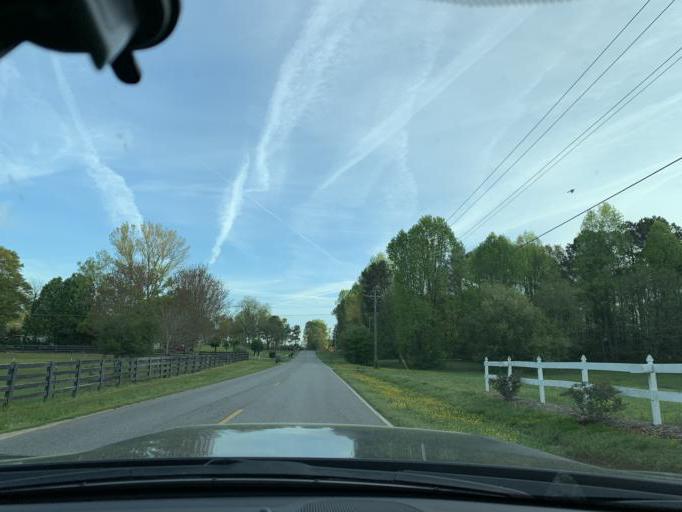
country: US
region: Georgia
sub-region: Forsyth County
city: Cumming
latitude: 34.2554
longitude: -84.1571
